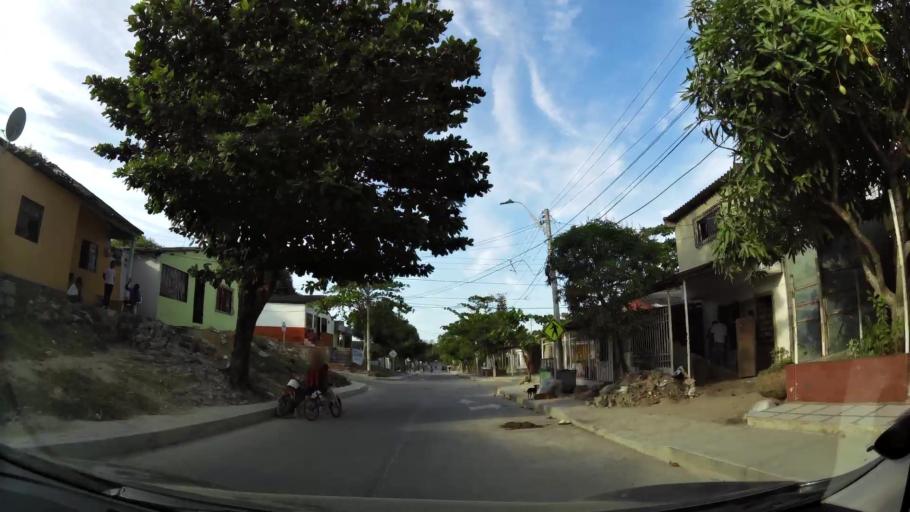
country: CO
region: Atlantico
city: Barranquilla
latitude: 10.9377
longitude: -74.8225
